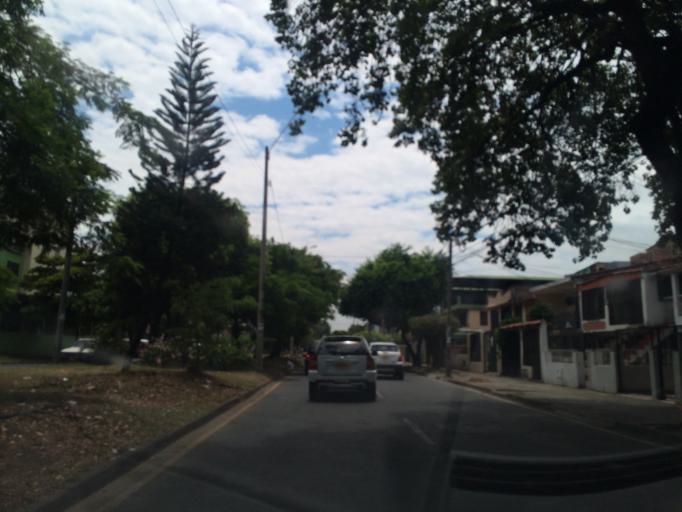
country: CO
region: Valle del Cauca
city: Cali
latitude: 3.4069
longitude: -76.5268
